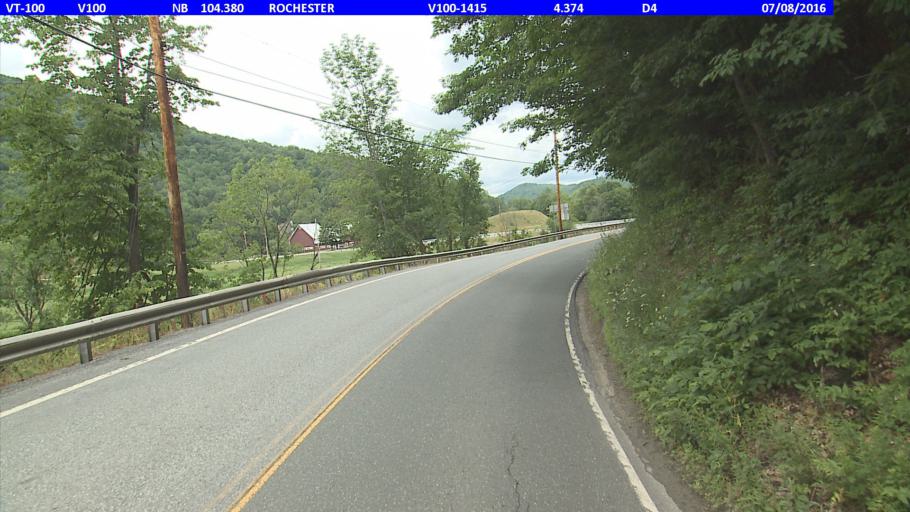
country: US
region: Vermont
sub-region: Orange County
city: Randolph
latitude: 43.8618
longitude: -72.8109
